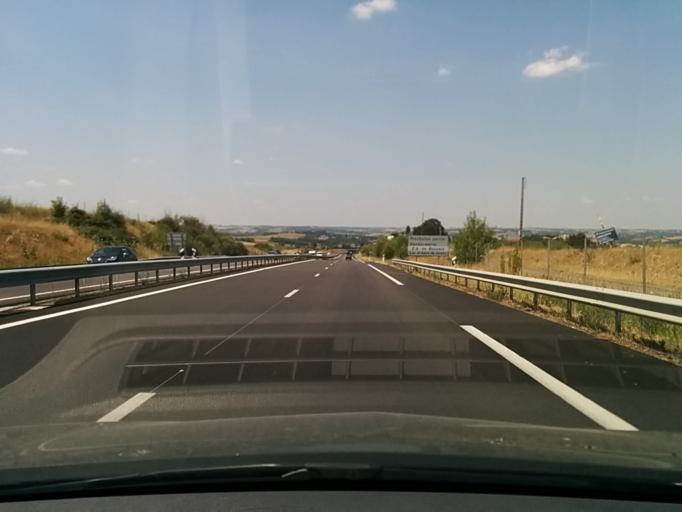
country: FR
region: Midi-Pyrenees
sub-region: Departement du Gers
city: Pujaudran
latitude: 43.5951
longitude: 1.1203
